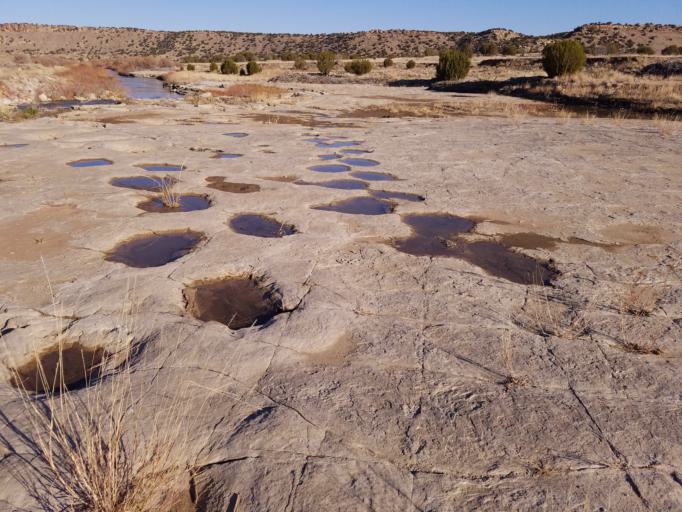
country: US
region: Colorado
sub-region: Otero County
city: La Junta
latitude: 37.6169
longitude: -103.5986
